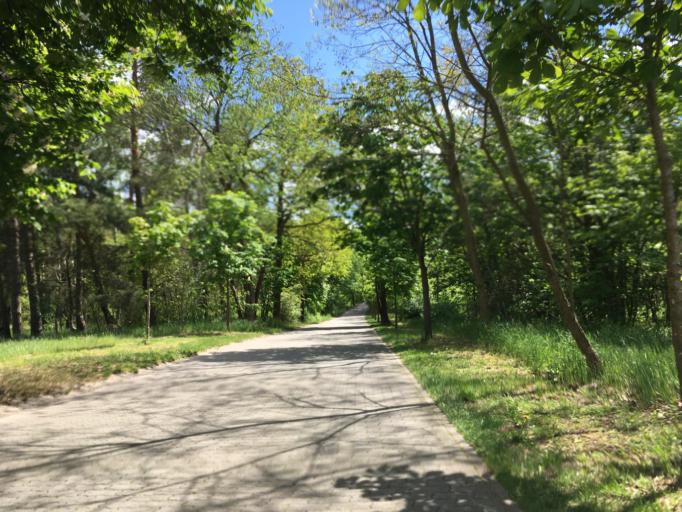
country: DE
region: Brandenburg
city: Biesenthal
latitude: 52.7487
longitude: 13.6493
